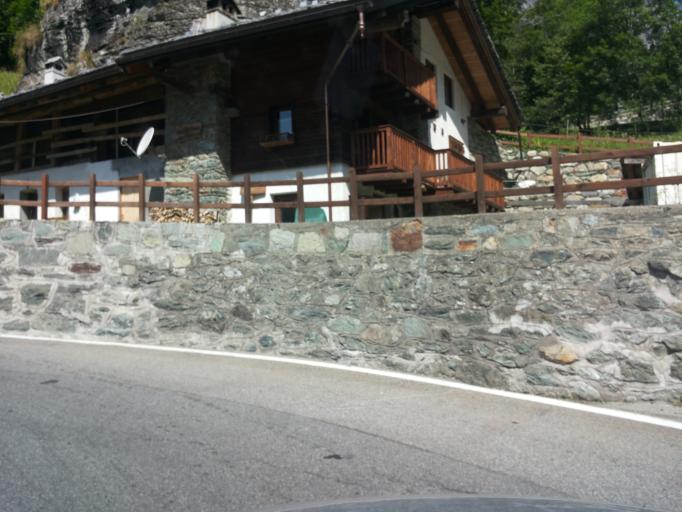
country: IT
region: Aosta Valley
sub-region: Valle d'Aosta
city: Gressoney-La-Trinite
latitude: 45.8028
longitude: 7.8229
